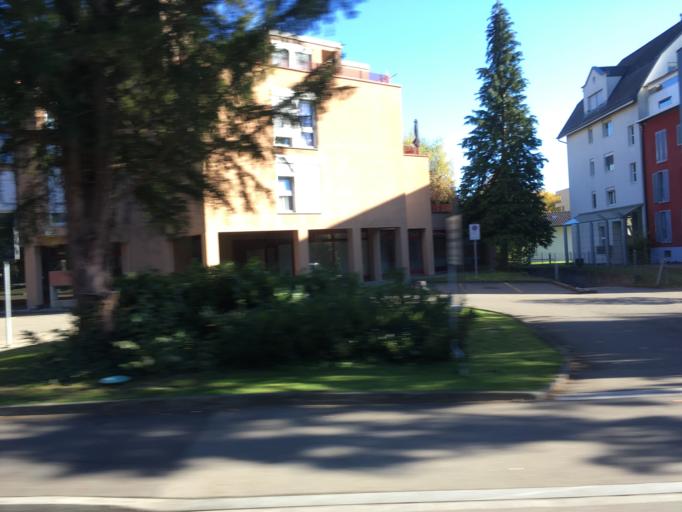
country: CH
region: Zurich
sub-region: Bezirk Hinwil
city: Wetzikon / Kempten
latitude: 47.3302
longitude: 8.8054
